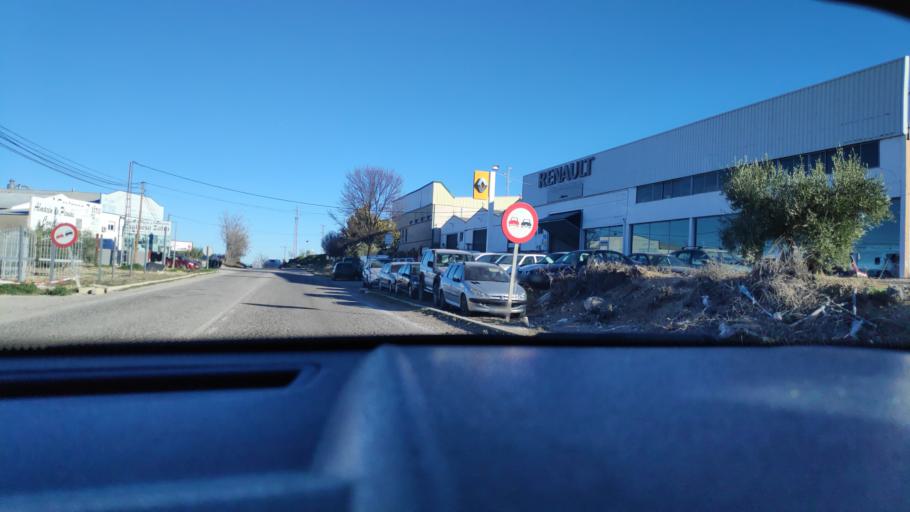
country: ES
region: Andalusia
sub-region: Provincia de Jaen
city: Mancha Real
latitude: 37.7924
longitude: -3.6070
